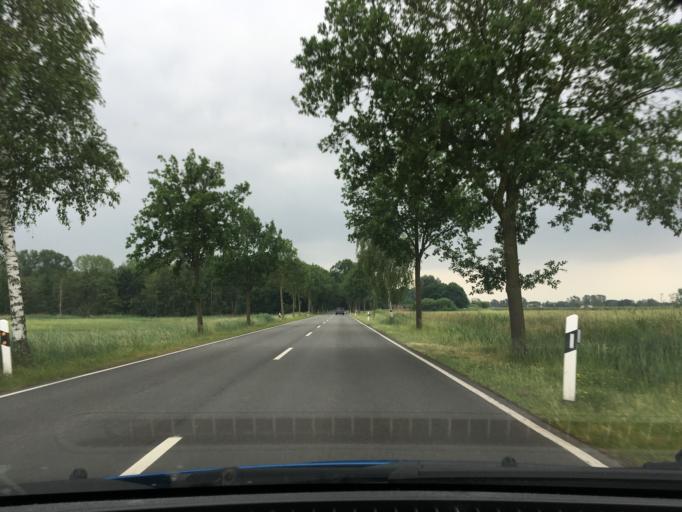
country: DE
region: Lower Saxony
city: Lubbow
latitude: 52.8959
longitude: 11.1790
